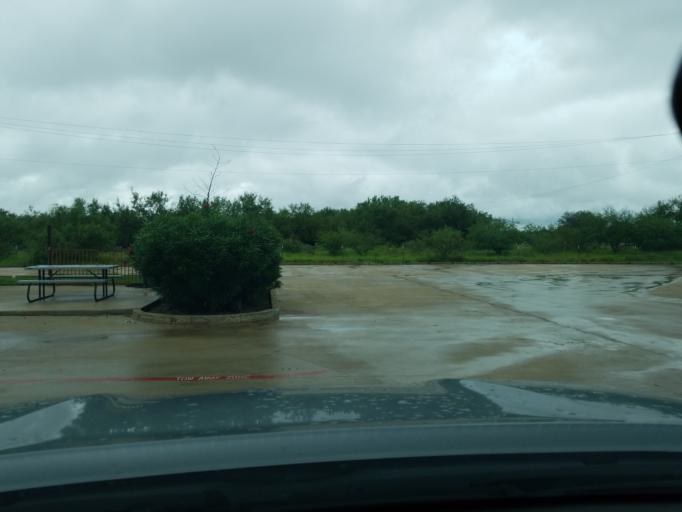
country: US
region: Texas
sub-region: Dimmit County
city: Carrizo Springs
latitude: 28.5305
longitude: -99.8322
